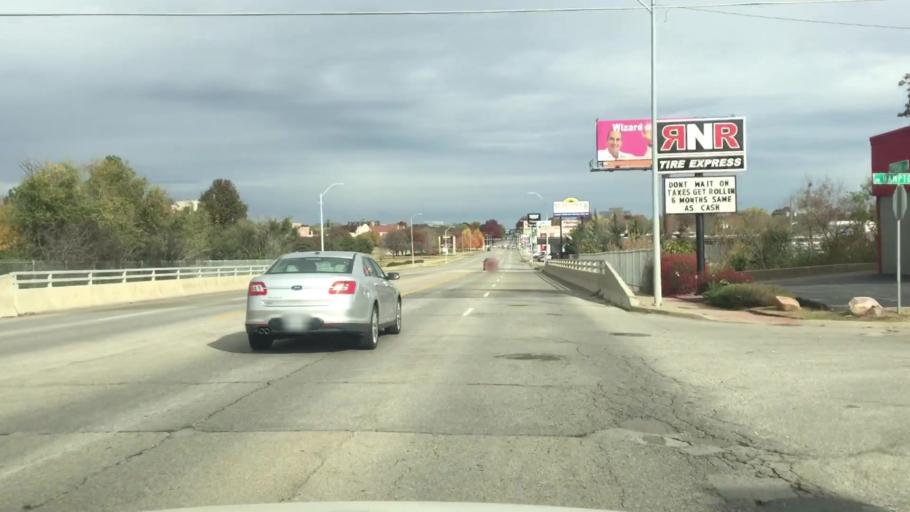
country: US
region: Kansas
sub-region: Shawnee County
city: Topeka
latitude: 39.0311
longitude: -95.6828
